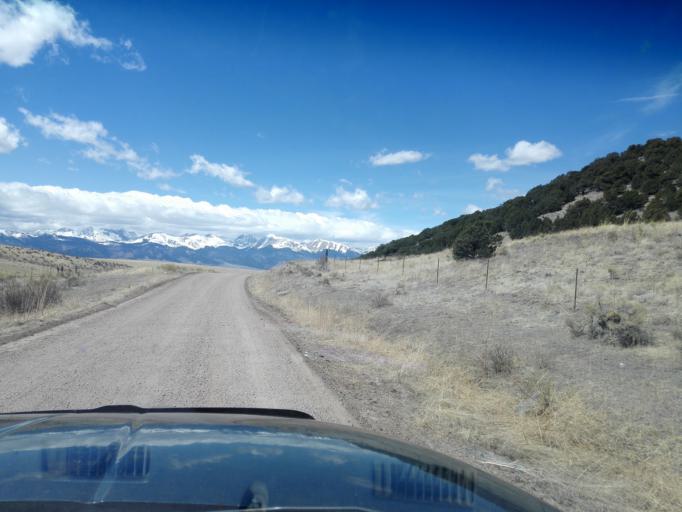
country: US
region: Colorado
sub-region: Custer County
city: Westcliffe
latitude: 37.9745
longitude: -105.2787
